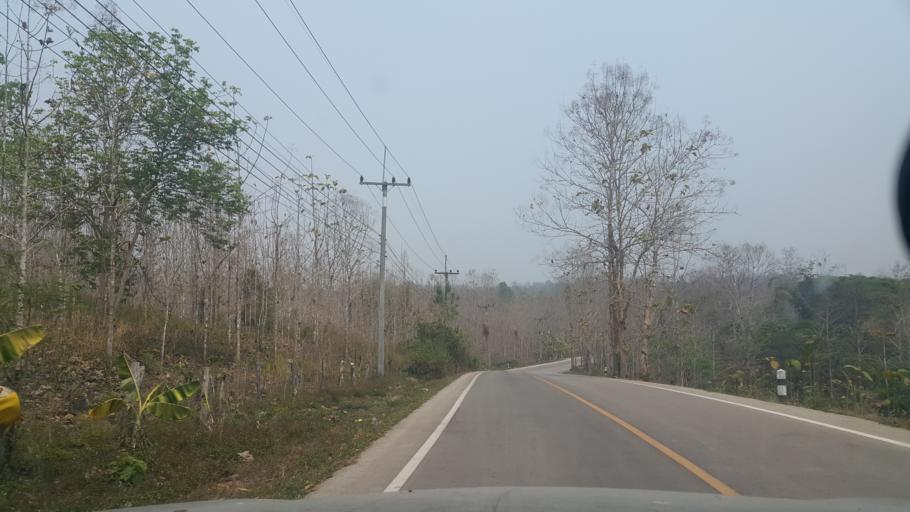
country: TH
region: Lampang
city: Soem Ngam
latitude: 18.1700
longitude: 99.1862
